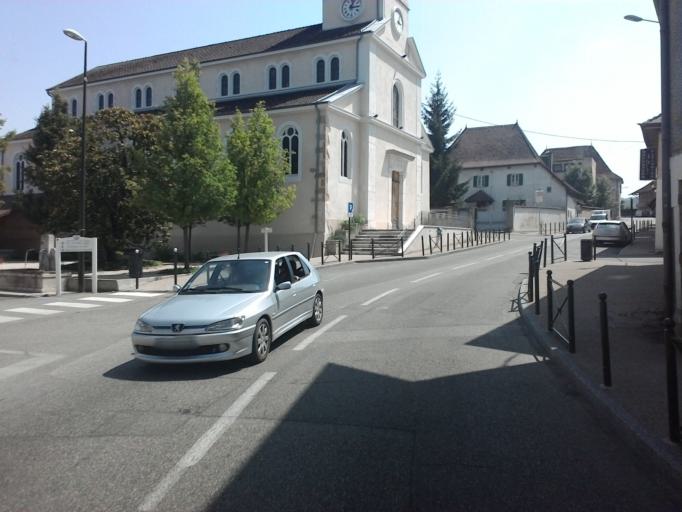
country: FR
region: Rhone-Alpes
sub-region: Departement de l'Isere
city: Les Abrets
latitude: 45.5352
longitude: 5.5863
